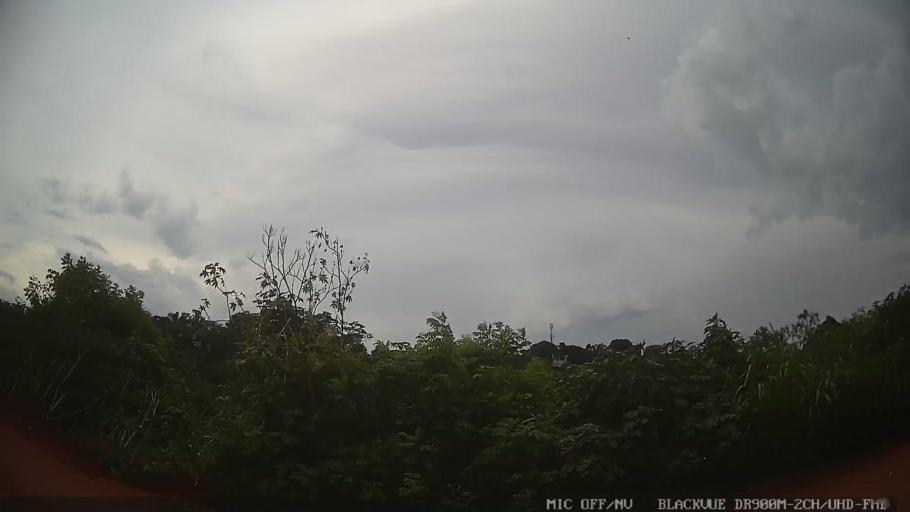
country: BR
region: Sao Paulo
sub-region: Itaquaquecetuba
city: Itaquaquecetuba
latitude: -23.4708
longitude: -46.2987
